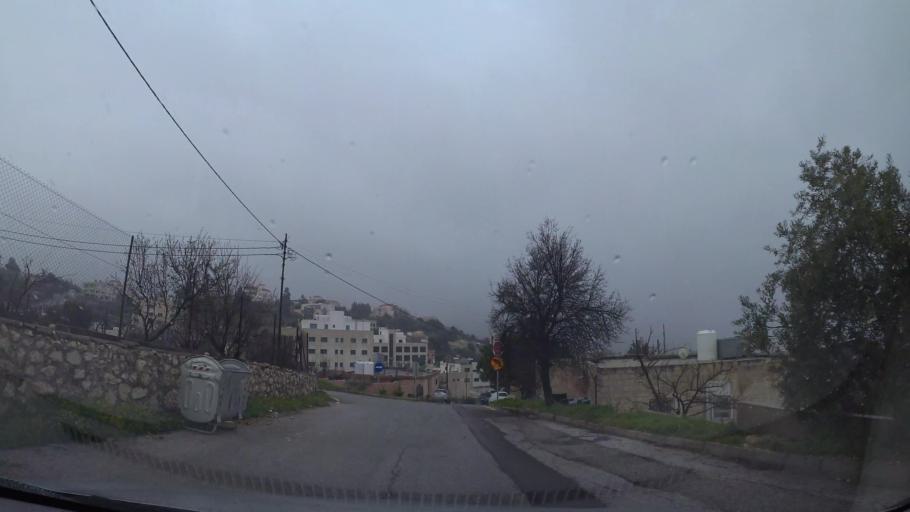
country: JO
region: Amman
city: Wadi as Sir
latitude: 32.0039
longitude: 35.7943
